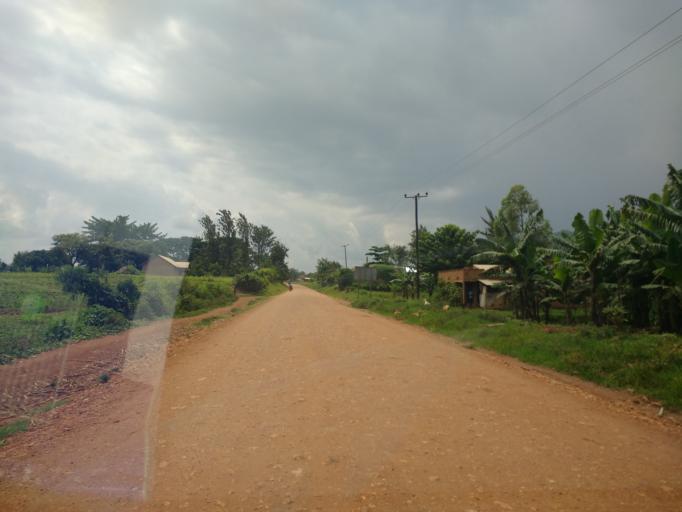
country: UG
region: Eastern Region
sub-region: Sironko District
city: Sironko
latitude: 1.3365
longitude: 34.2979
